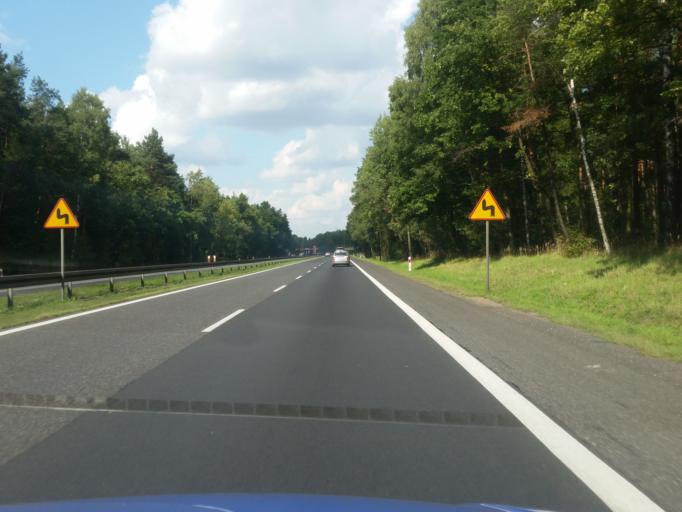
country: PL
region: Silesian Voivodeship
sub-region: Powiat czestochowski
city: Kamienica Polska
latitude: 50.6562
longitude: 19.1313
